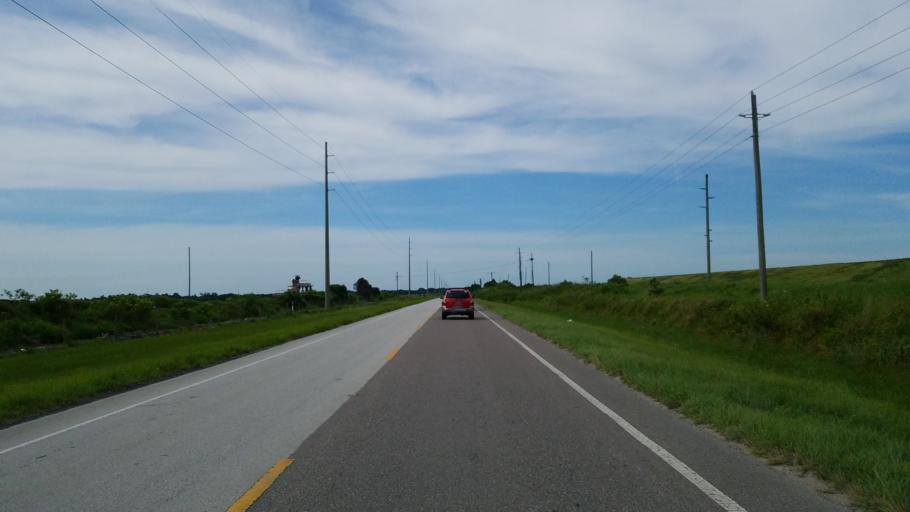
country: US
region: Florida
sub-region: Hillsborough County
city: Balm
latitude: 27.6574
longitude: -82.1463
